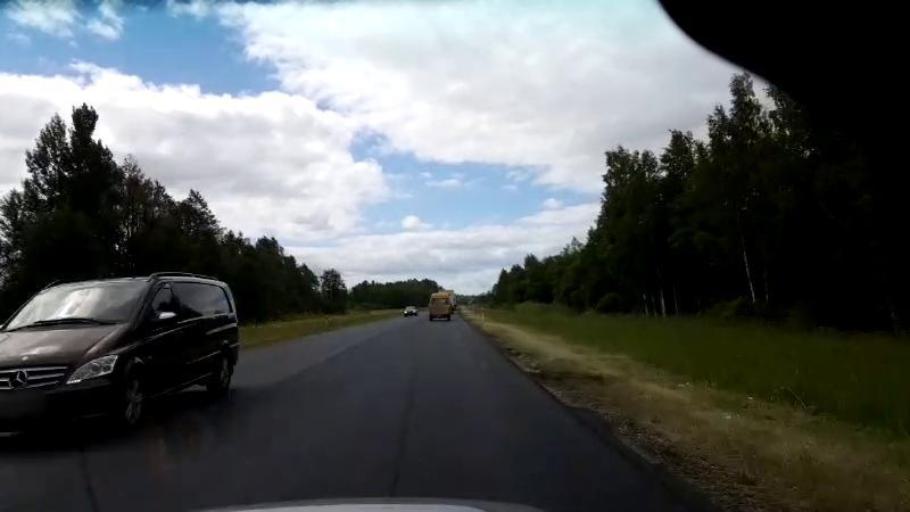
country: LV
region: Salacgrivas
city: Ainazi
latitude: 57.9044
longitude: 24.4143
